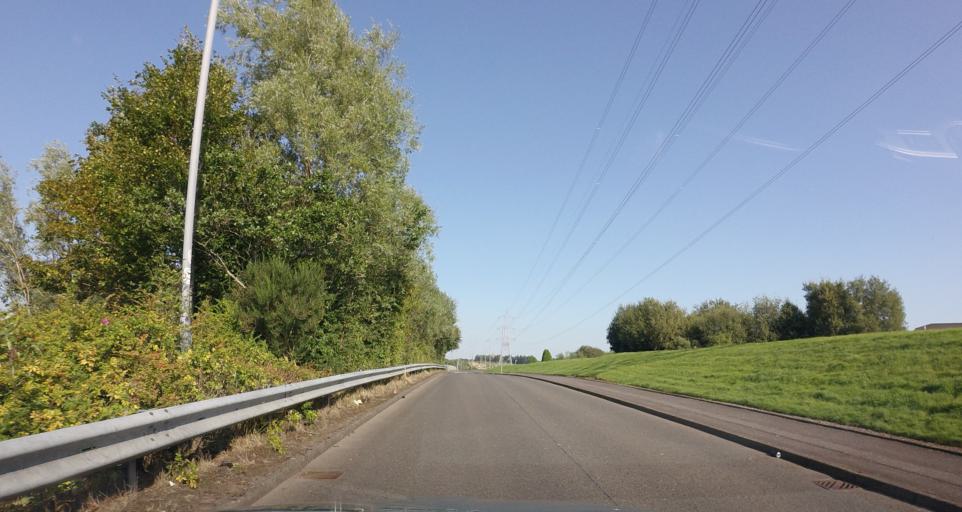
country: GB
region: Scotland
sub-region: South Lanarkshire
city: East Kilbride
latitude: 55.7406
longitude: -4.1969
